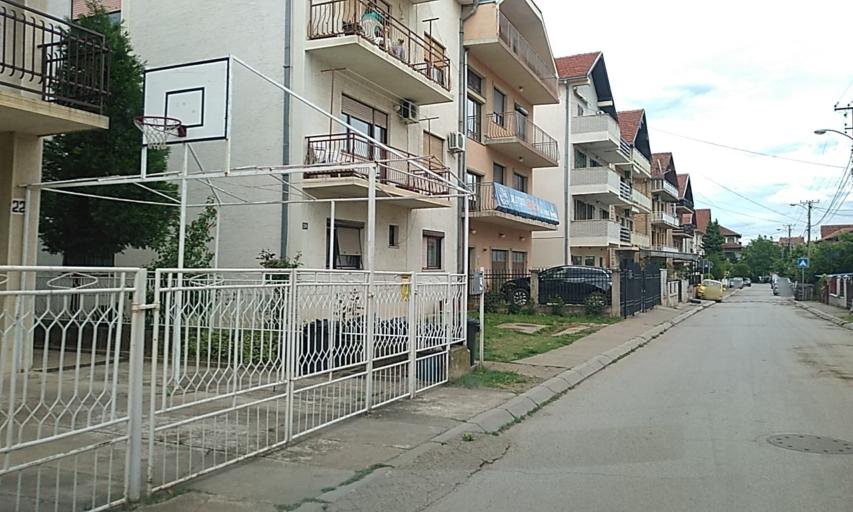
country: RS
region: Central Serbia
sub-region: Nisavski Okrug
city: Nis
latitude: 43.3378
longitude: 21.9103
